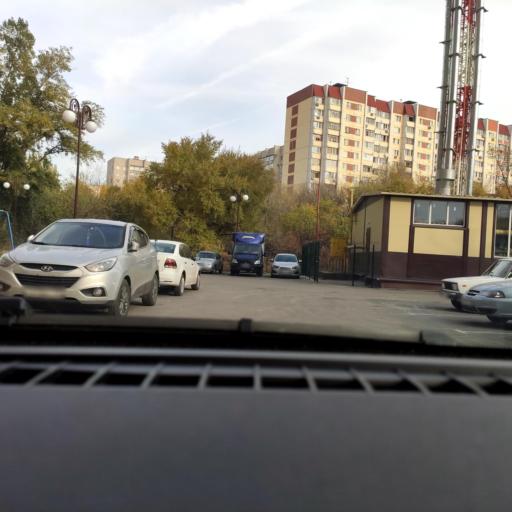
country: RU
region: Voronezj
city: Voronezh
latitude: 51.7061
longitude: 39.2724
